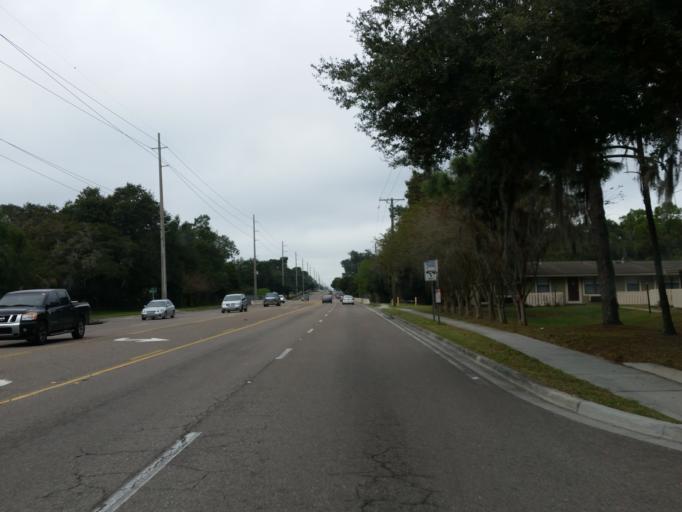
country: US
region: Florida
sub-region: Hillsborough County
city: Riverview
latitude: 27.8937
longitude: -82.2965
